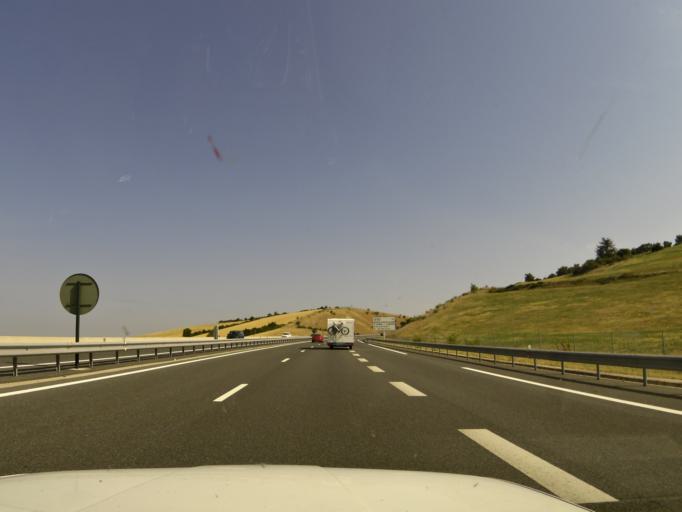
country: FR
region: Midi-Pyrenees
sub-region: Departement de l'Aveyron
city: Creissels
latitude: 44.1309
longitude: 3.0294
